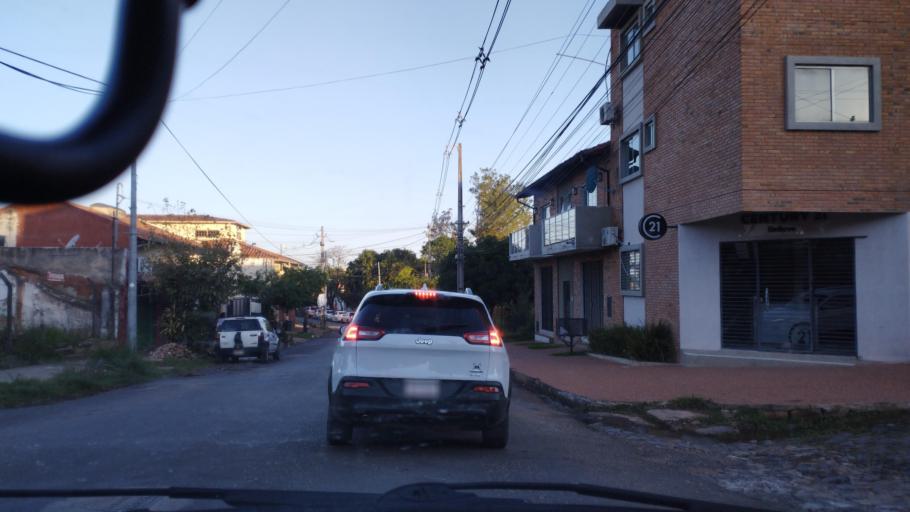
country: PY
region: Central
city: Fernando de la Mora
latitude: -25.2981
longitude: -57.5537
